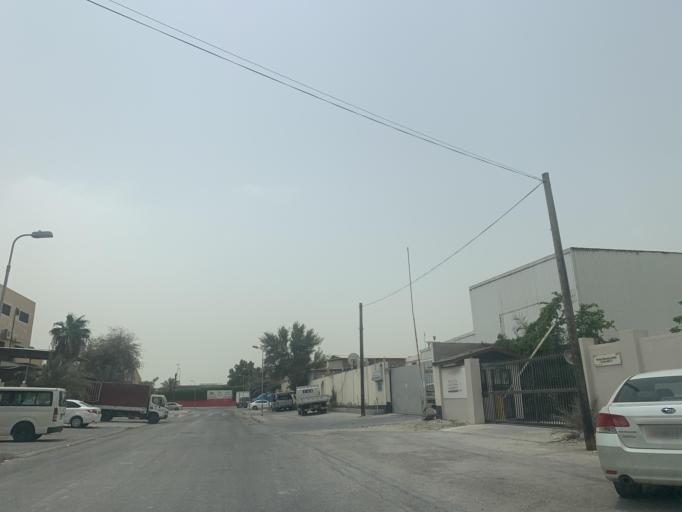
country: BH
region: Northern
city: Sitrah
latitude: 26.1754
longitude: 50.6010
